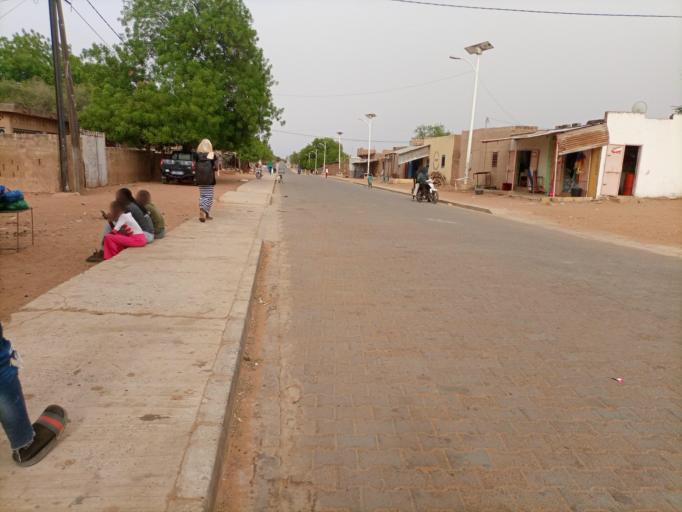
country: SN
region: Louga
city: Ndibene Dahra
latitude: 15.4003
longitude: -15.1170
